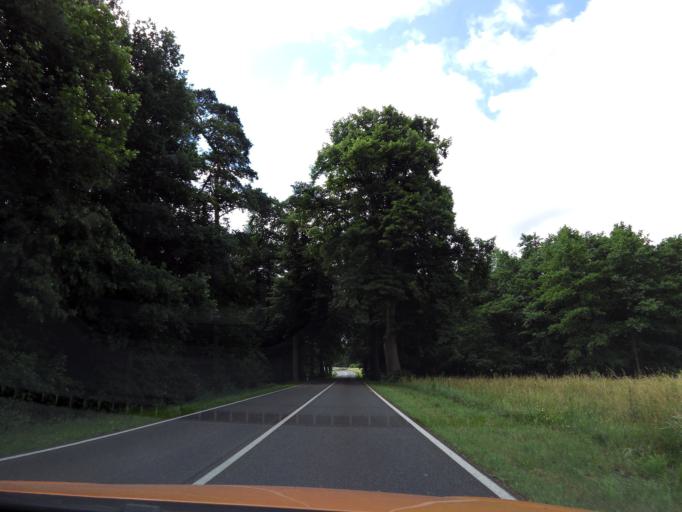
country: DE
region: Mecklenburg-Vorpommern
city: Muhl Rosin
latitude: 53.7608
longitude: 12.2464
